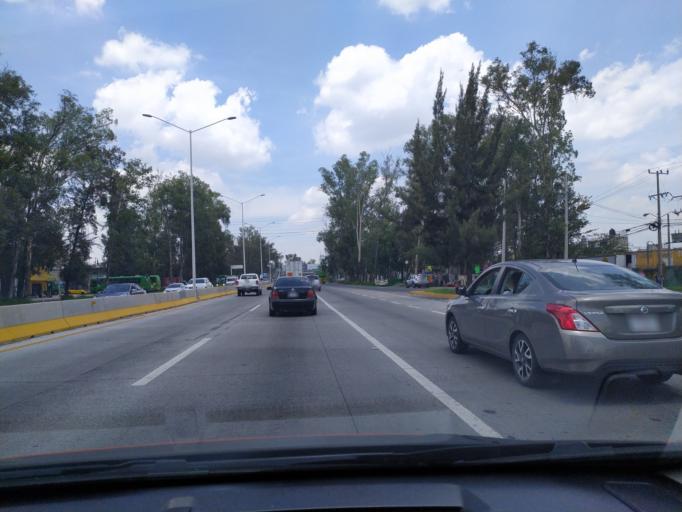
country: MX
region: Jalisco
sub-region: San Pedro Tlaquepaque
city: Paseo del Prado
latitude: 20.6007
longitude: -103.3960
